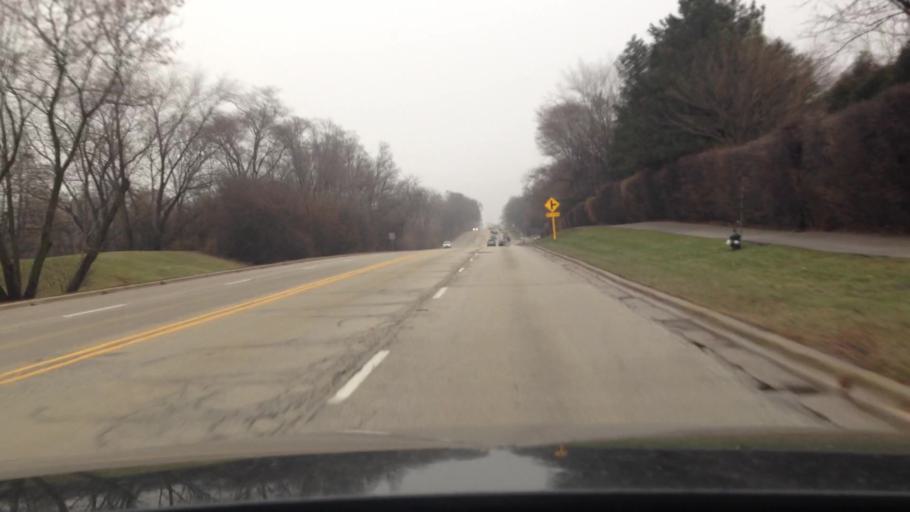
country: US
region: Illinois
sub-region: DuPage County
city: Oakbrook Terrace
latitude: 41.8314
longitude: -87.9837
